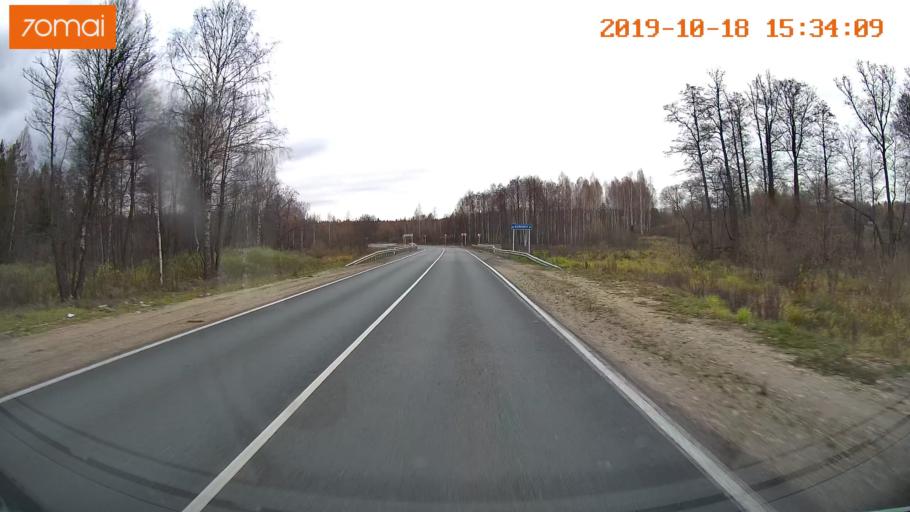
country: RU
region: Vladimir
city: Anopino
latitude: 55.8512
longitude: 40.6450
